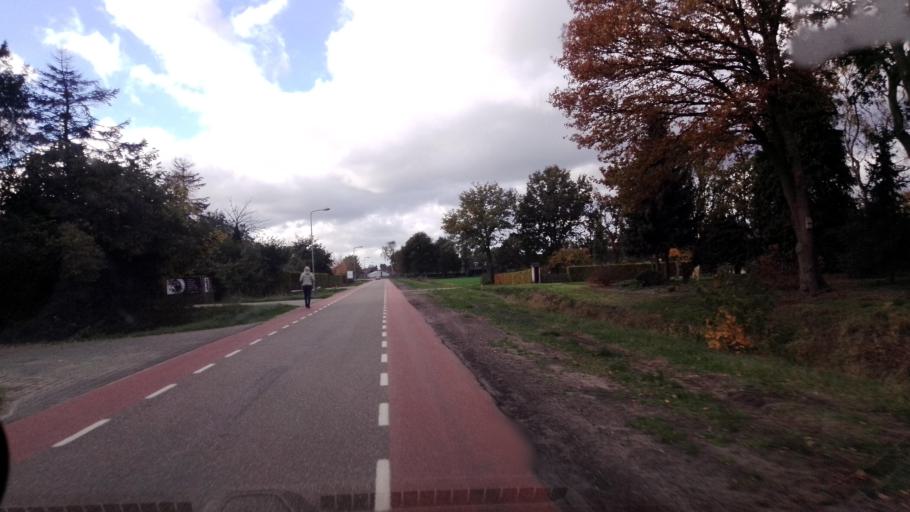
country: NL
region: Limburg
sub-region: Gemeente Venray
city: Venray
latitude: 51.4957
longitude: 5.9200
